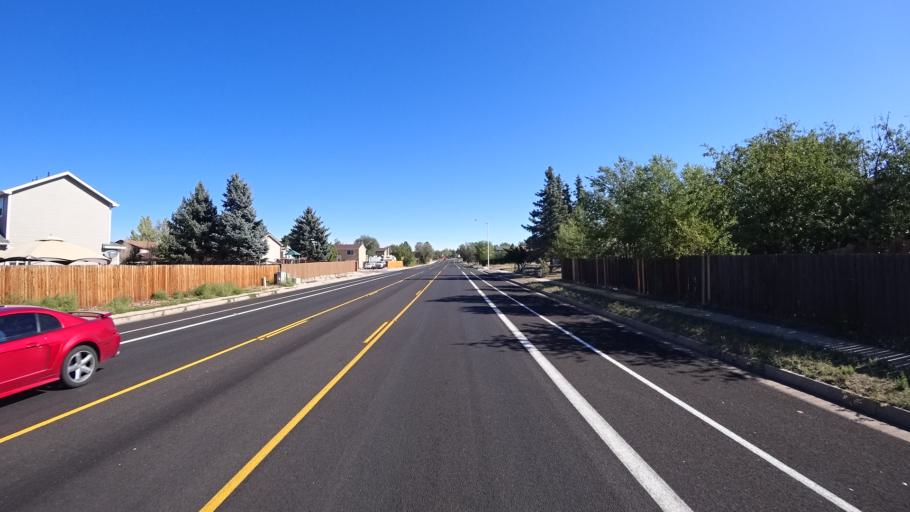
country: US
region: Colorado
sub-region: El Paso County
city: Stratmoor
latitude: 38.8119
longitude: -104.7389
